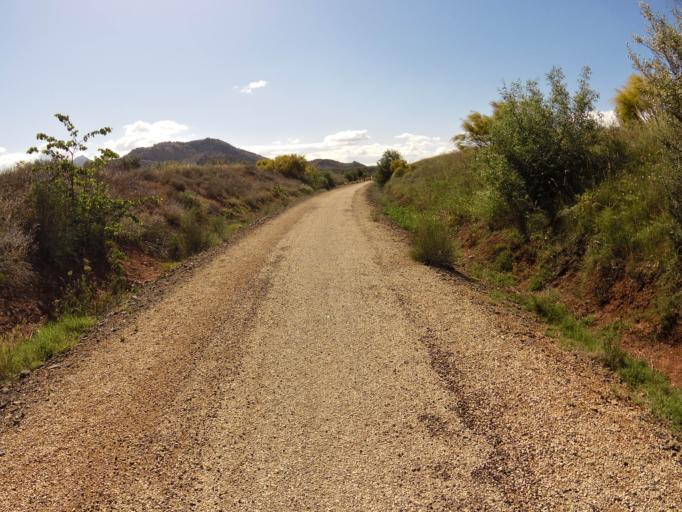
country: ES
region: Andalusia
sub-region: Provincia de Jaen
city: Alcaudete
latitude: 37.6027
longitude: -4.1448
